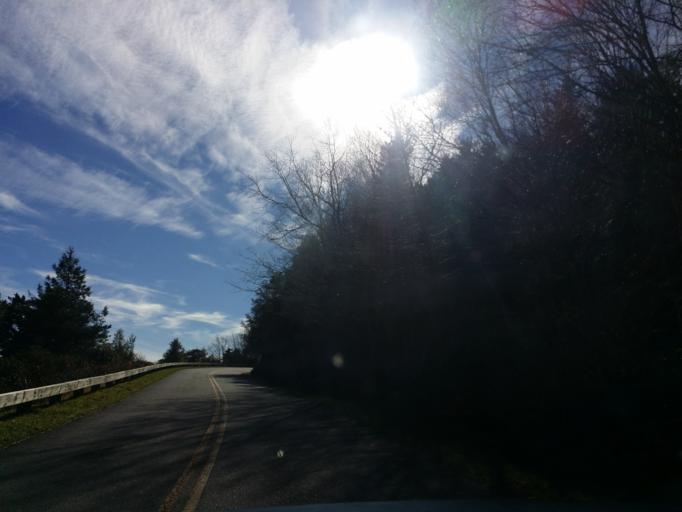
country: US
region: North Carolina
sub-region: Buncombe County
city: Black Mountain
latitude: 35.7237
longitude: -82.2111
